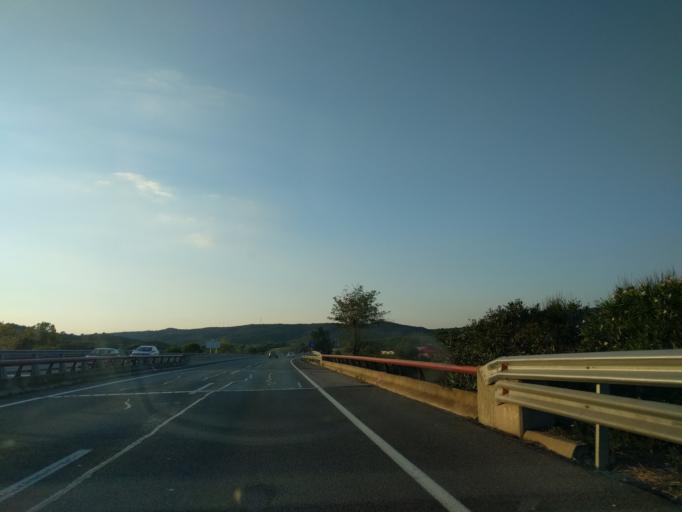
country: ES
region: Catalonia
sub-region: Provincia de Girona
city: Santa Cristina d'Aro
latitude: 41.8187
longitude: 2.9803
